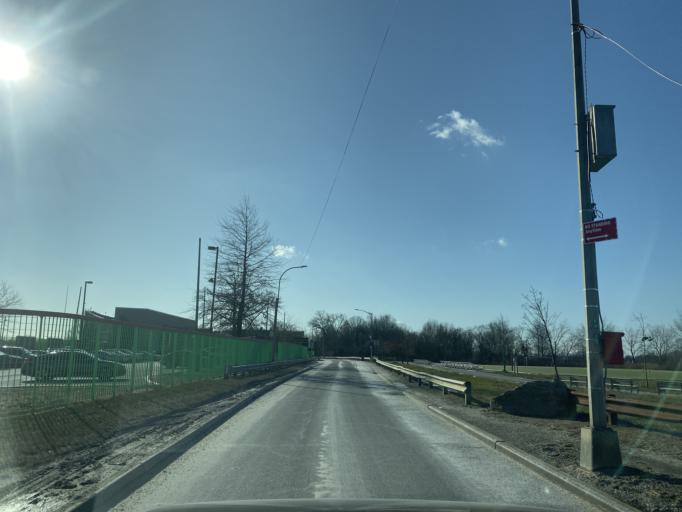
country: US
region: New York
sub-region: Bronx
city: The Bronx
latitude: 40.8159
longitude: -73.8372
